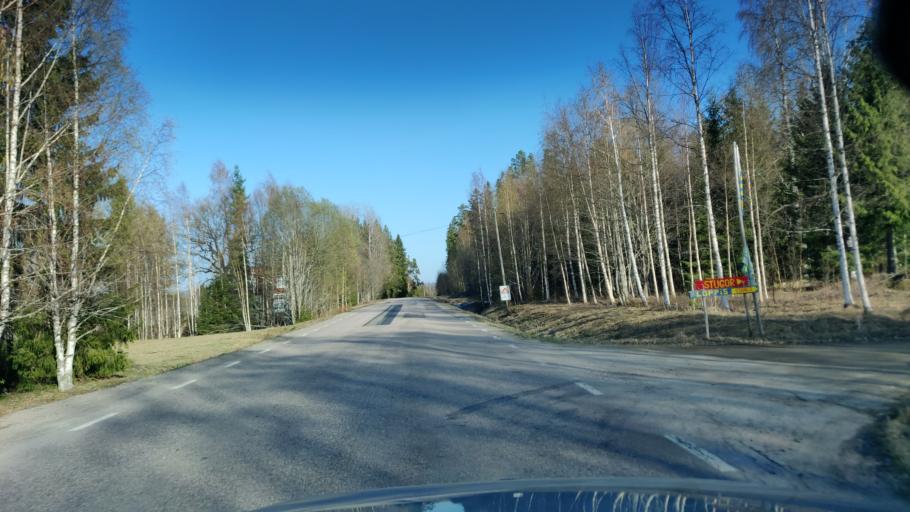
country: SE
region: Vaermland
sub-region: Munkfors Kommun
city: Munkfors
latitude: 59.9702
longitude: 13.4571
